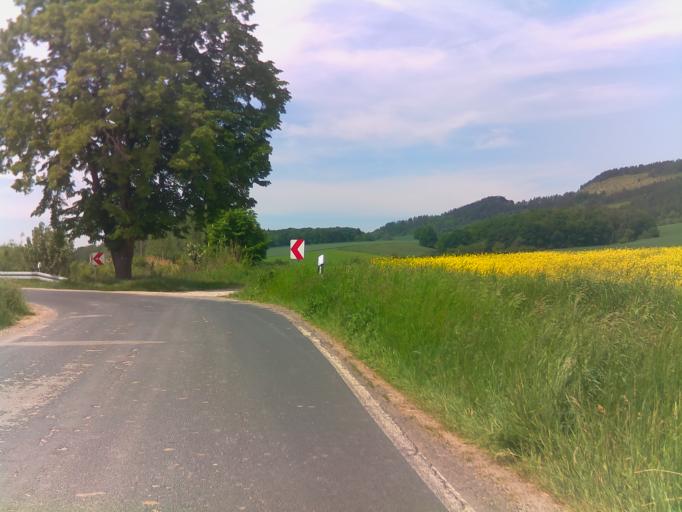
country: DE
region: Thuringia
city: Rittersdorf
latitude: 50.7613
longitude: 11.1979
